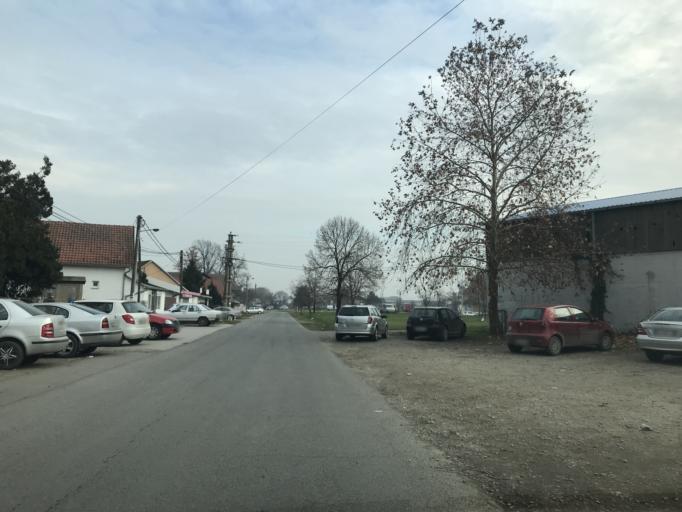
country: RS
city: Veternik
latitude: 45.2503
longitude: 19.7537
